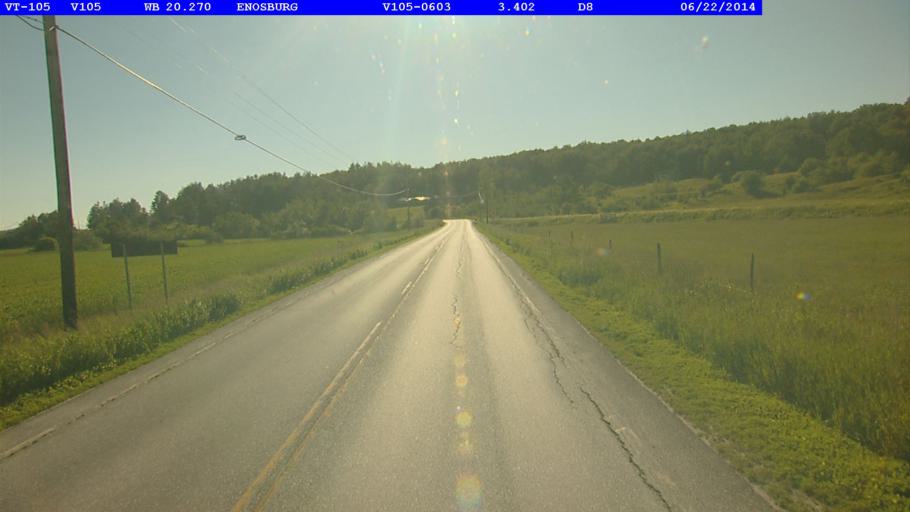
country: US
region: Vermont
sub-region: Franklin County
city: Enosburg Falls
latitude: 44.9210
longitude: -72.7608
